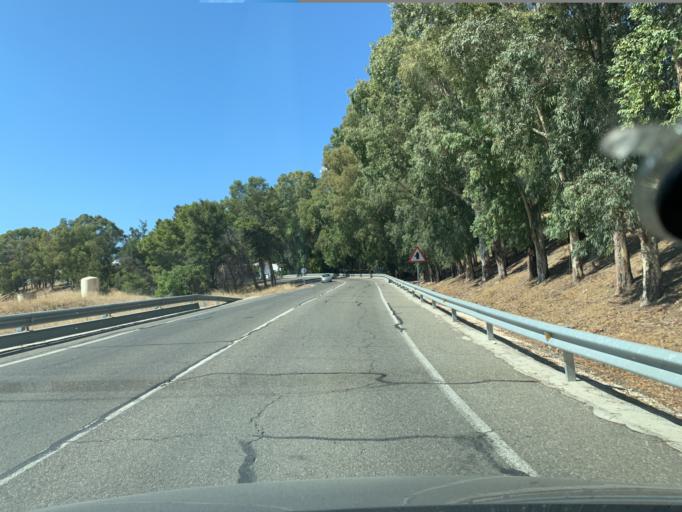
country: ES
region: Andalusia
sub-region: Provincia de Sevilla
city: Carmona
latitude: 37.4687
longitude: -5.6310
